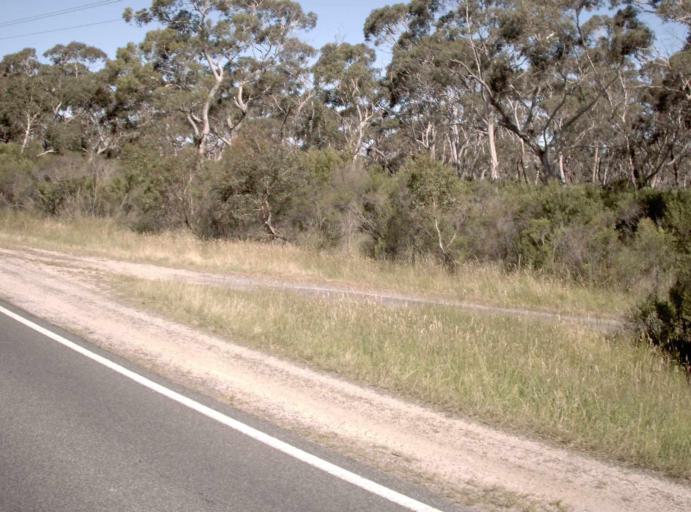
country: AU
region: Victoria
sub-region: Latrobe
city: Morwell
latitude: -38.6324
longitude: 146.5547
